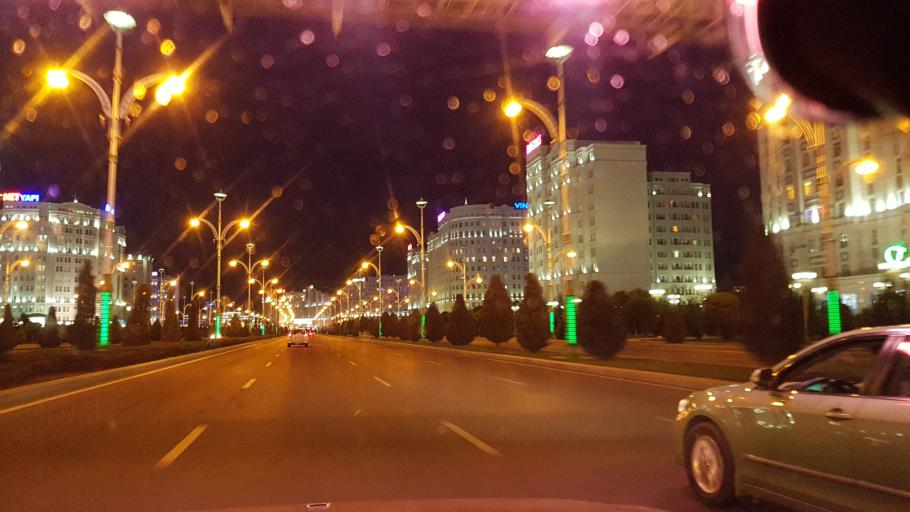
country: TM
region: Ahal
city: Ashgabat
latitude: 37.9023
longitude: 58.3431
